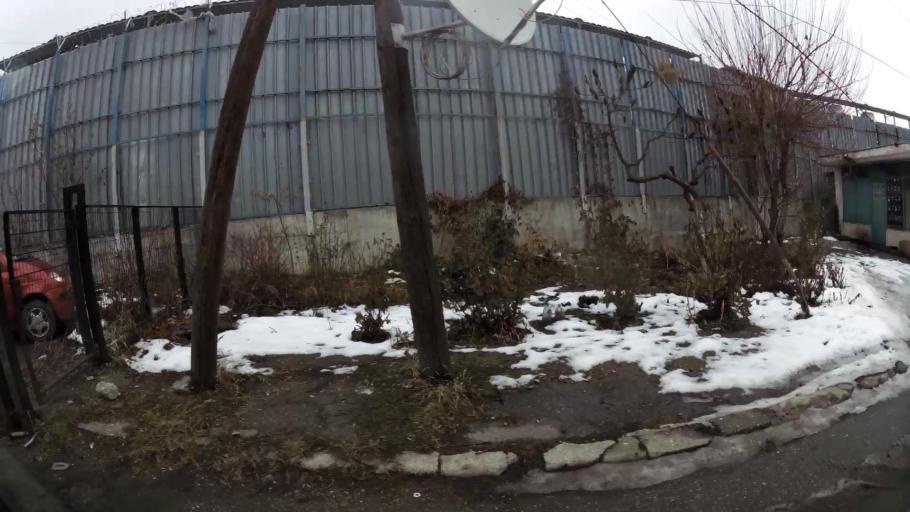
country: RO
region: Ilfov
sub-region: Comuna Popesti-Leordeni
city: Popesti-Leordeni
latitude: 44.4078
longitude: 26.1386
